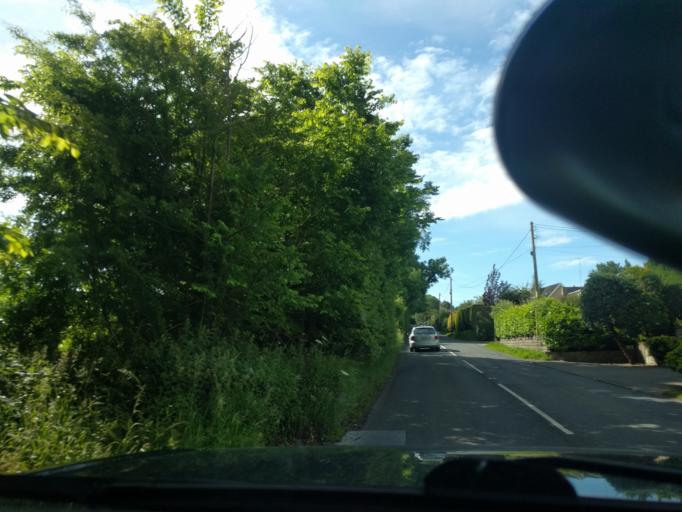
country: GB
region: England
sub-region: Wiltshire
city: Bradford-on-Avon
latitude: 51.3658
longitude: -2.2358
